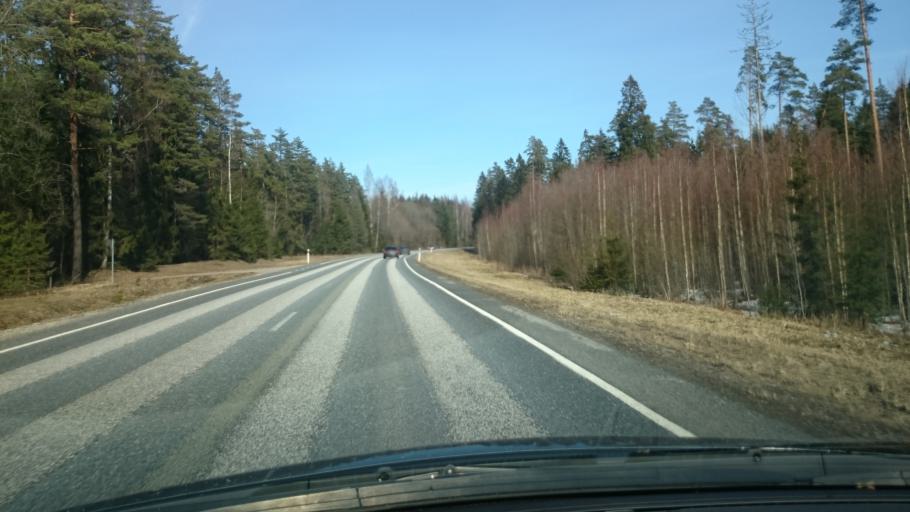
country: EE
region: Jaervamaa
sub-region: Tueri vald
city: Sarevere
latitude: 58.7394
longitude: 25.3016
